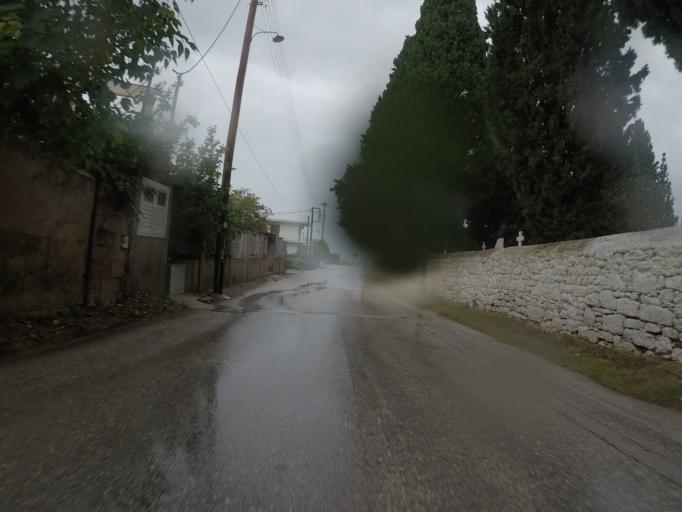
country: GR
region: Peloponnese
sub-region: Nomos Korinthias
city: Arkhaia Korinthos
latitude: 37.9107
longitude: 22.8843
